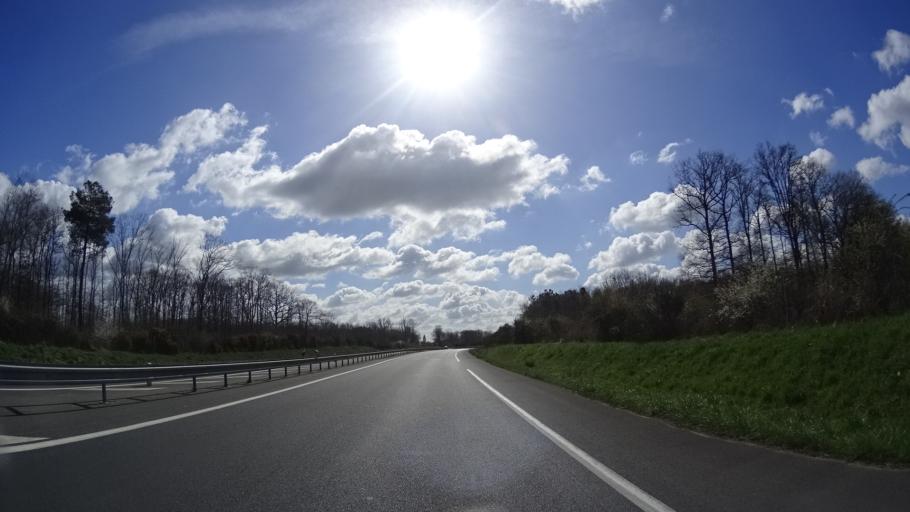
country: FR
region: Pays de la Loire
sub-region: Departement de Maine-et-Loire
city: Saint-Jean
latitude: 47.3046
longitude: -0.3925
